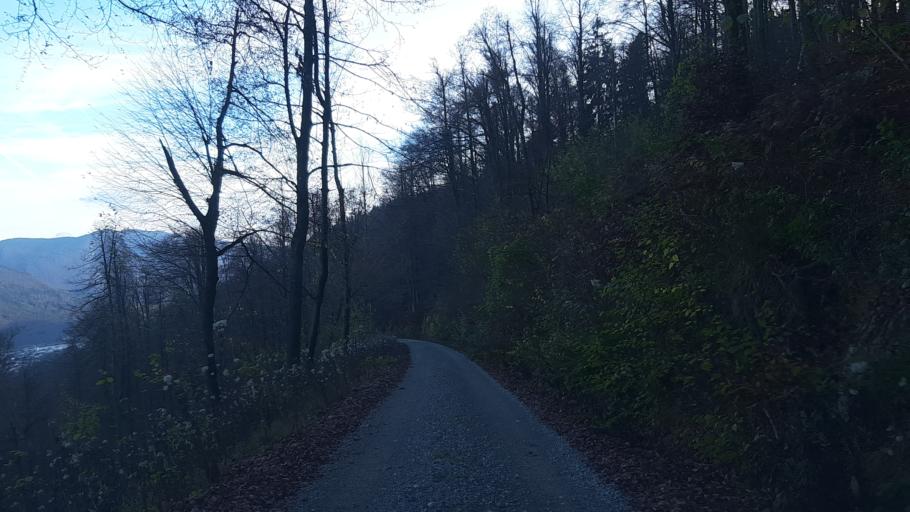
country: SI
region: Borovnica
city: Borovnica
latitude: 45.9300
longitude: 14.3379
